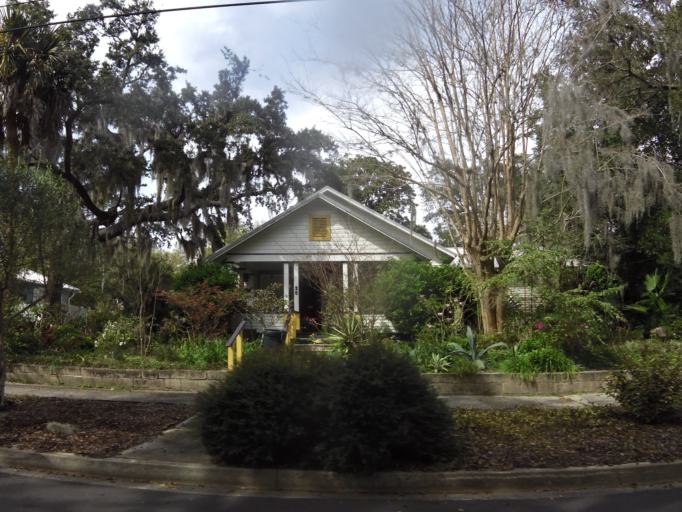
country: US
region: Florida
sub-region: Saint Johns County
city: Saint Augustine
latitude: 29.9161
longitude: -81.3195
